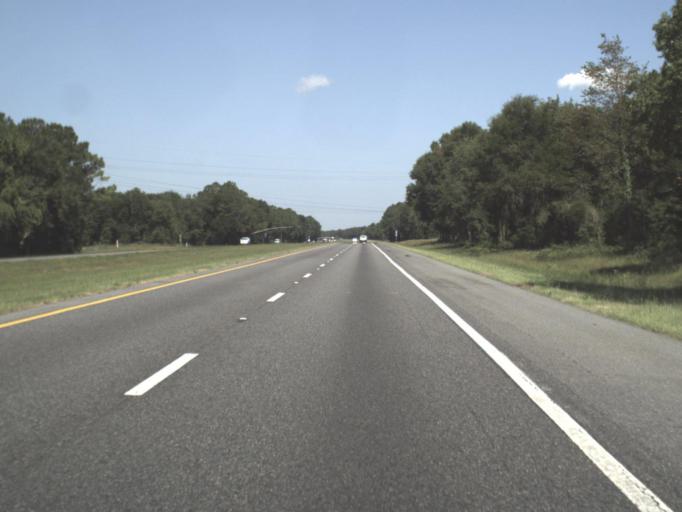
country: US
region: Florida
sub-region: Suwannee County
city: Live Oak
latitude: 30.3516
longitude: -83.1622
